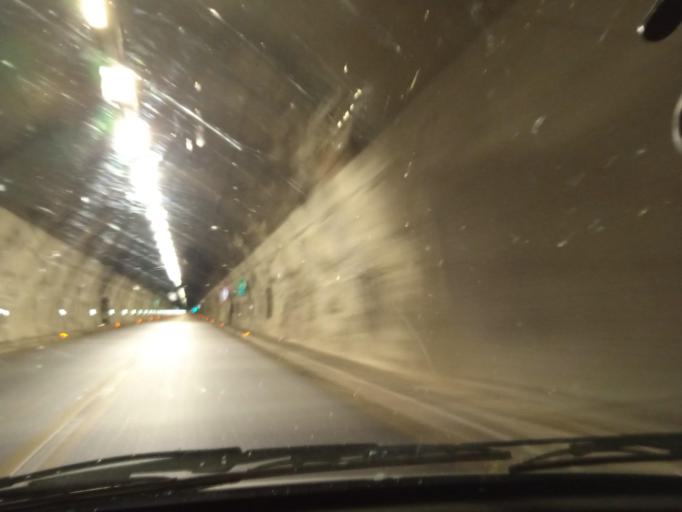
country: IT
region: Sicily
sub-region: Messina
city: Capo d'Orlando
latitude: 38.1387
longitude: 14.7428
